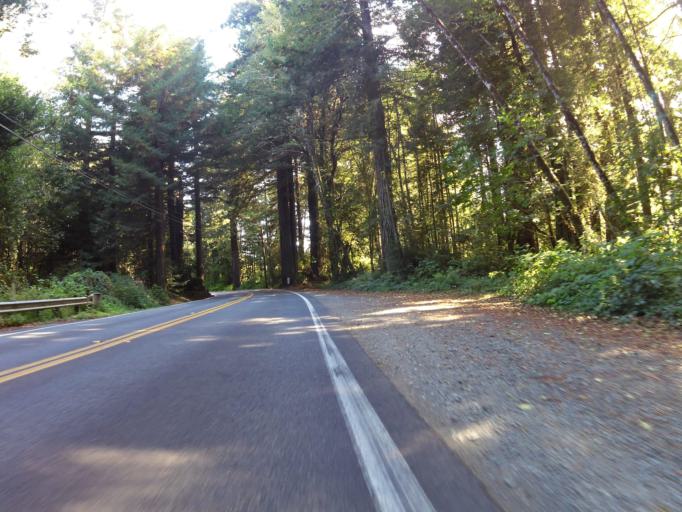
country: US
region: California
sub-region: Del Norte County
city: Bertsch-Oceanview
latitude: 41.8454
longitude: -124.1162
